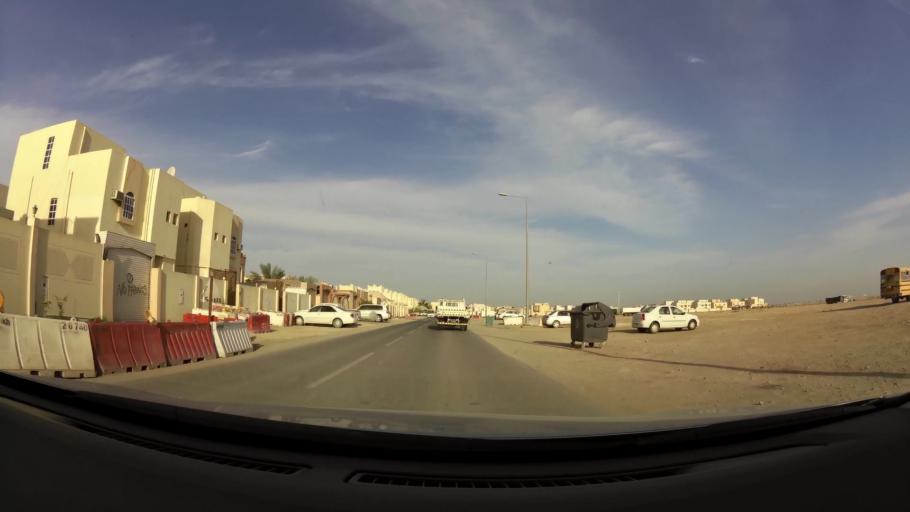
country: QA
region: Al Wakrah
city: Al Wakrah
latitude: 25.1443
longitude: 51.6080
